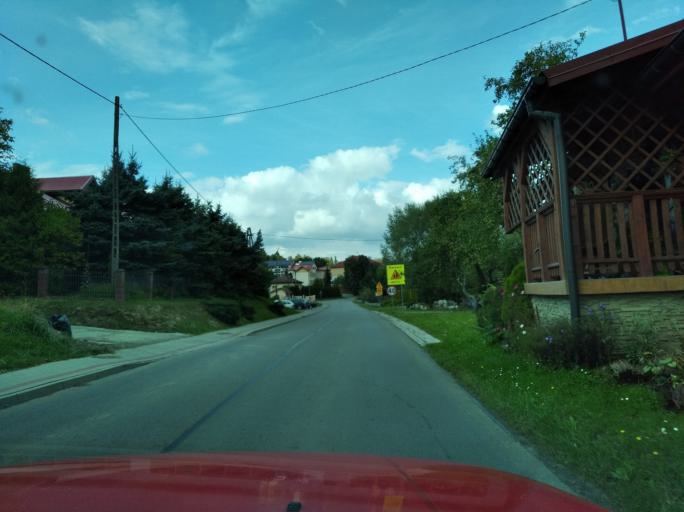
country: PL
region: Subcarpathian Voivodeship
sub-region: Powiat rzeszowski
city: Tyczyn
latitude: 49.9395
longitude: 22.0198
